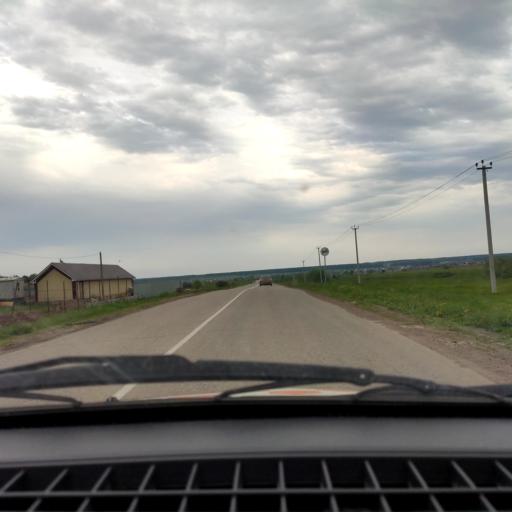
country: RU
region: Bashkortostan
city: Avdon
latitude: 54.5696
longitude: 55.7571
